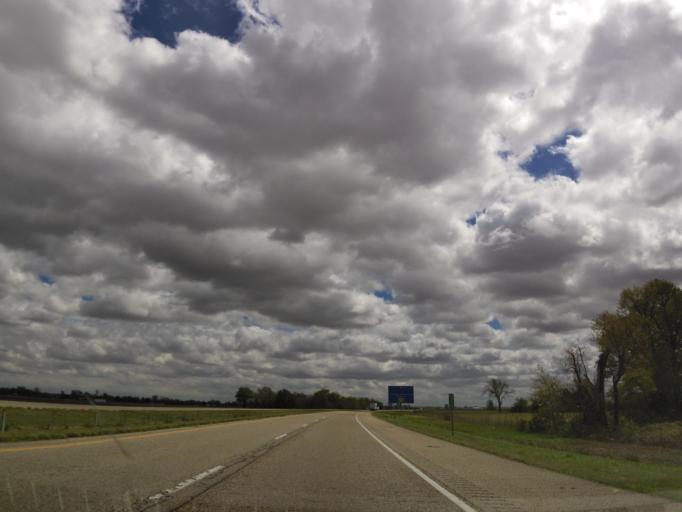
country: US
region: Arkansas
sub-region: Poinsett County
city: Trumann
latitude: 35.6446
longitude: -90.5142
